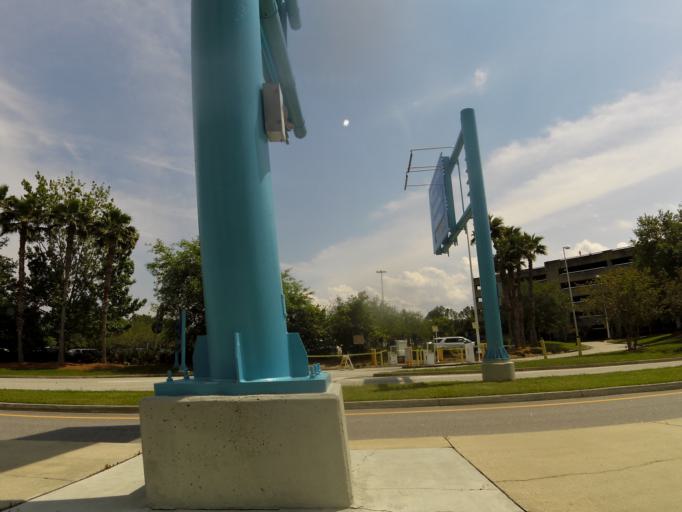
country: US
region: Florida
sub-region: Nassau County
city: Nassau Village-Ratliff
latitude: 30.4928
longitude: -81.6812
